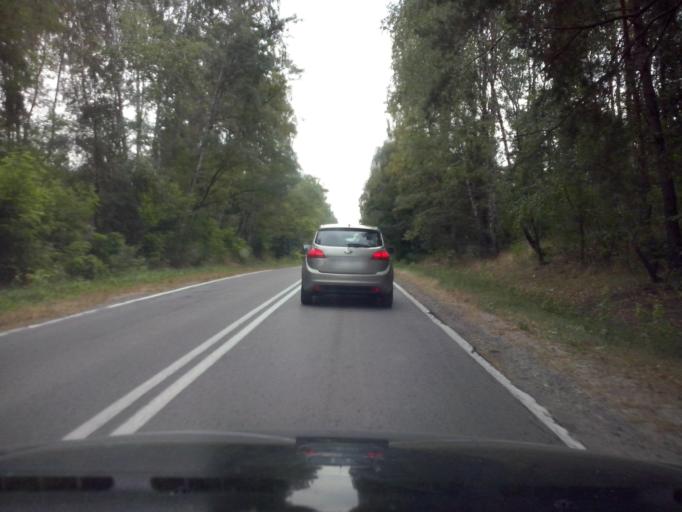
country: PL
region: Swietokrzyskie
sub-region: Powiat kielecki
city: Rakow
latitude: 50.7007
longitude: 21.0565
